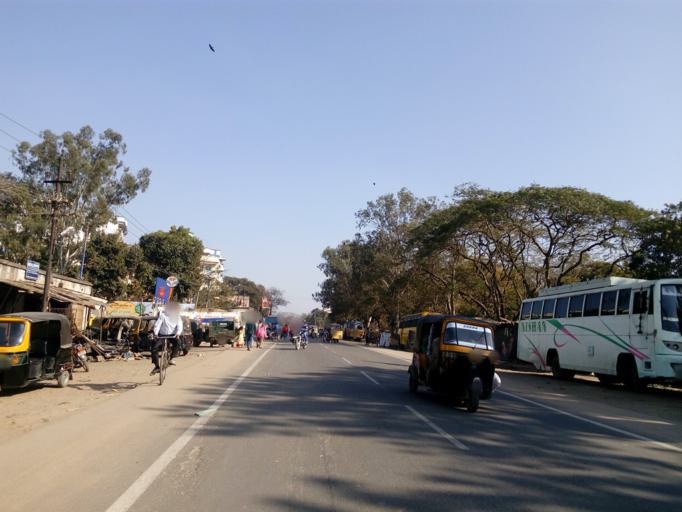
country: IN
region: Jharkhand
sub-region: Ranchi
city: Ranchi
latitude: 23.3614
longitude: 85.3534
